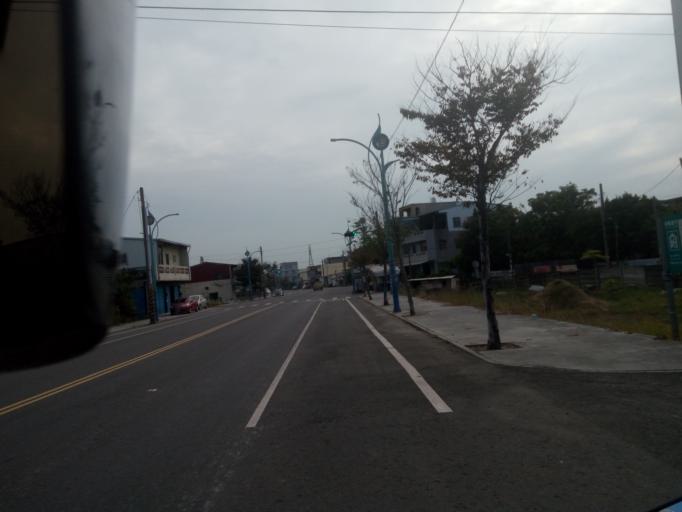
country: TW
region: Taiwan
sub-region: Chiayi
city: Taibao
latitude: 23.4858
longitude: 120.3354
